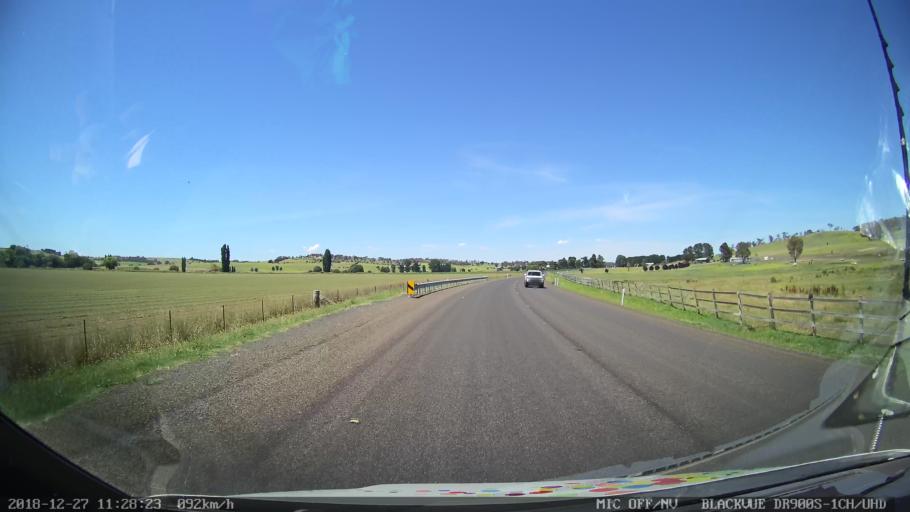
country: AU
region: New South Wales
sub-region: Bathurst Regional
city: Perthville
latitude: -33.4755
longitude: 149.5639
